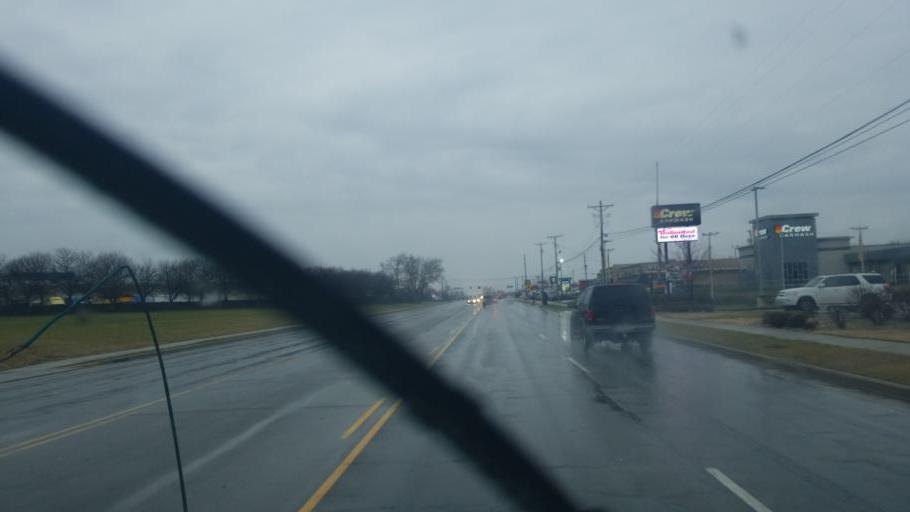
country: US
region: Indiana
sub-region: Bartholomew County
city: Columbus
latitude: 39.2145
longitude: -85.8815
